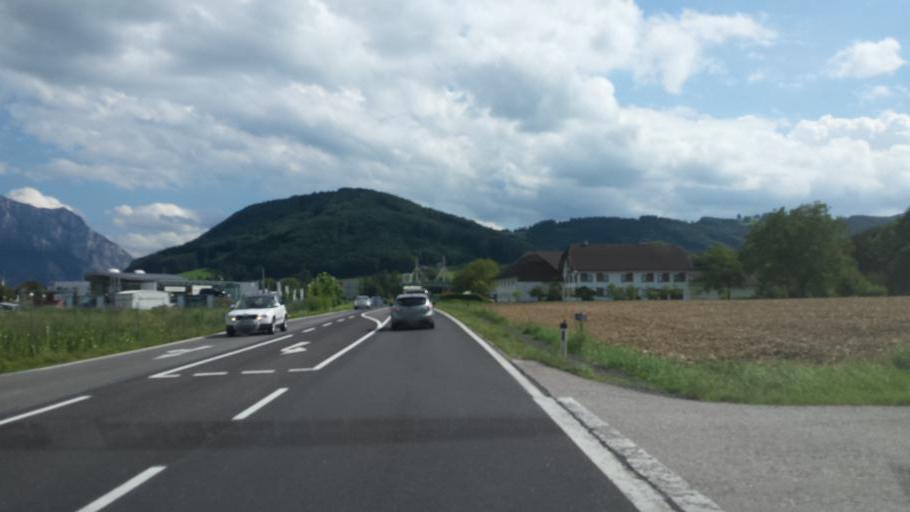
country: AT
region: Upper Austria
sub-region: Politischer Bezirk Gmunden
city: Altmunster
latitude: 47.9403
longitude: 13.7570
